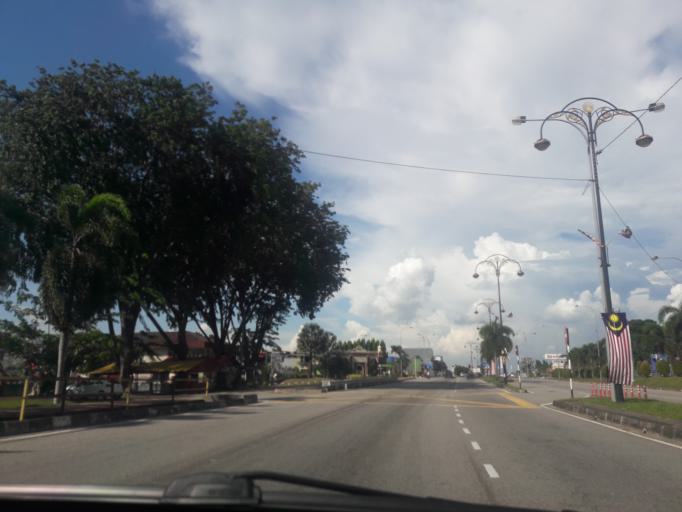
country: MY
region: Kedah
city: Sungai Petani
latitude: 5.6191
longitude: 100.4734
